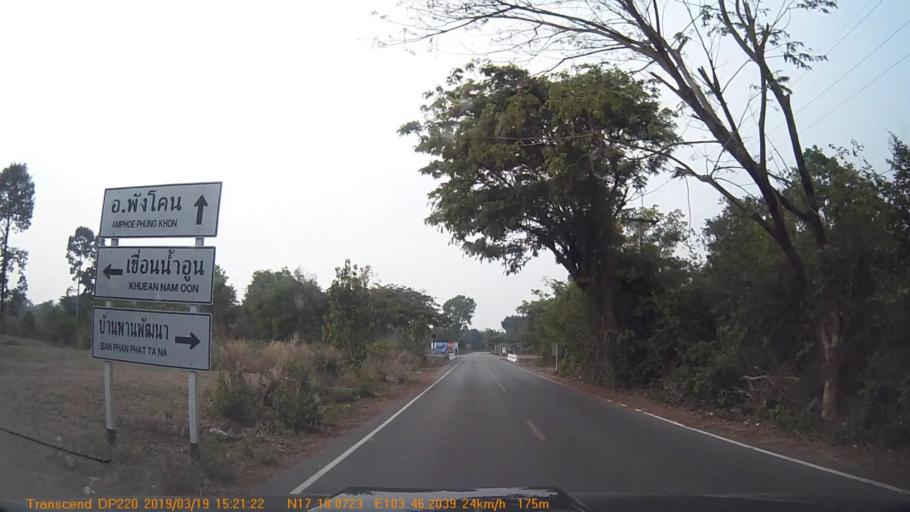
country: TH
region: Sakon Nakhon
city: Phanna Nikhom
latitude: 17.3013
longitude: 103.7700
